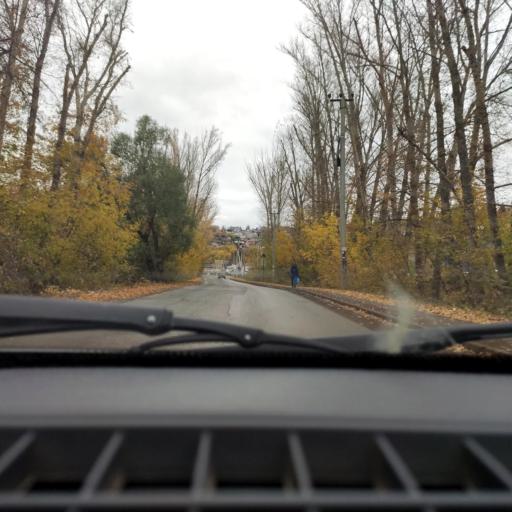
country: RU
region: Bashkortostan
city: Ufa
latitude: 54.6953
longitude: 55.9684
